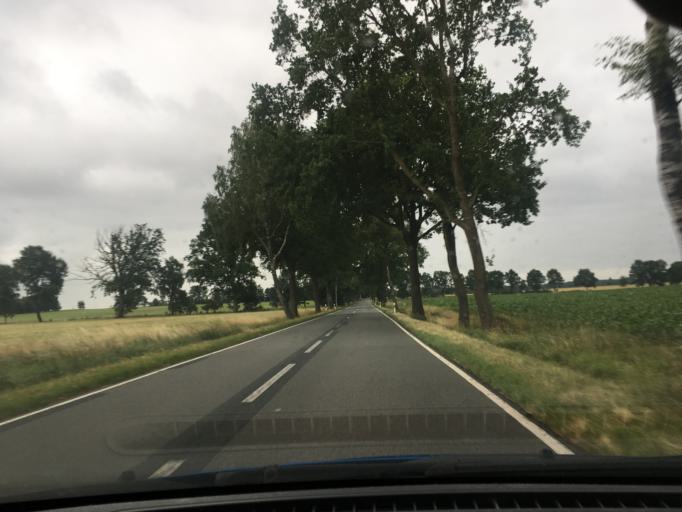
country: DE
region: Lower Saxony
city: Egestorf
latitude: 53.2073
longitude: 10.0705
